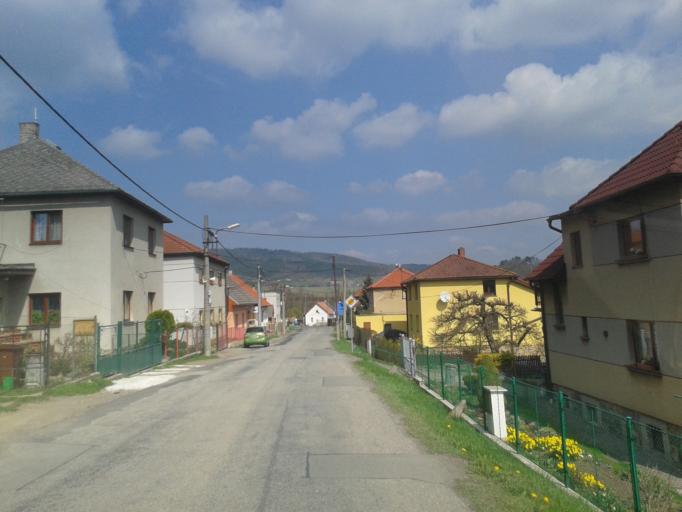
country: CZ
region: Central Bohemia
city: Zdice
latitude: 49.8980
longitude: 13.9607
